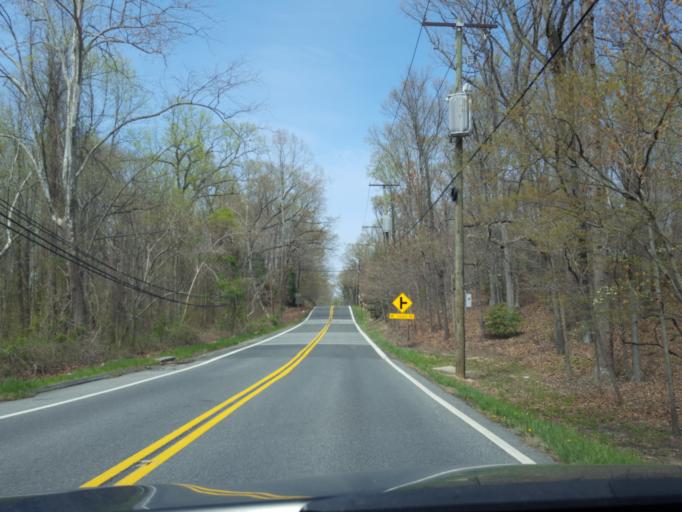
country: US
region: Maryland
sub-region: Prince George's County
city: Croom
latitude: 38.7654
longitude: -76.7554
